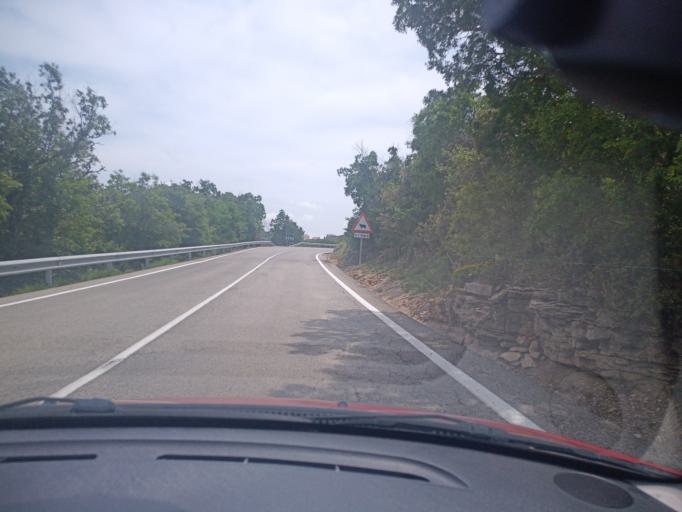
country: ES
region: Valencia
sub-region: Provincia de Castello
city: Ares del Maestre
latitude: 40.4600
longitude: -0.1499
